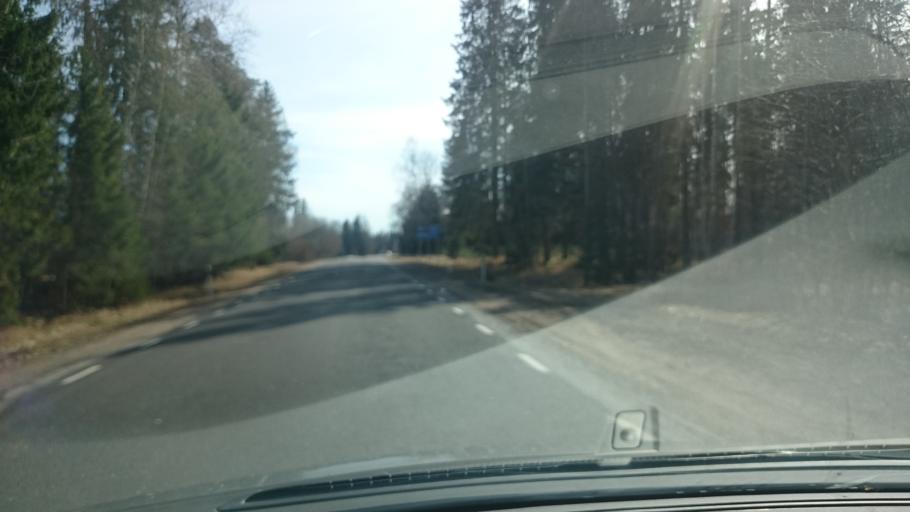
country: EE
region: Paernumaa
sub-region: Vaendra vald (alev)
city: Vandra
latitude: 58.6291
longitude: 24.9204
